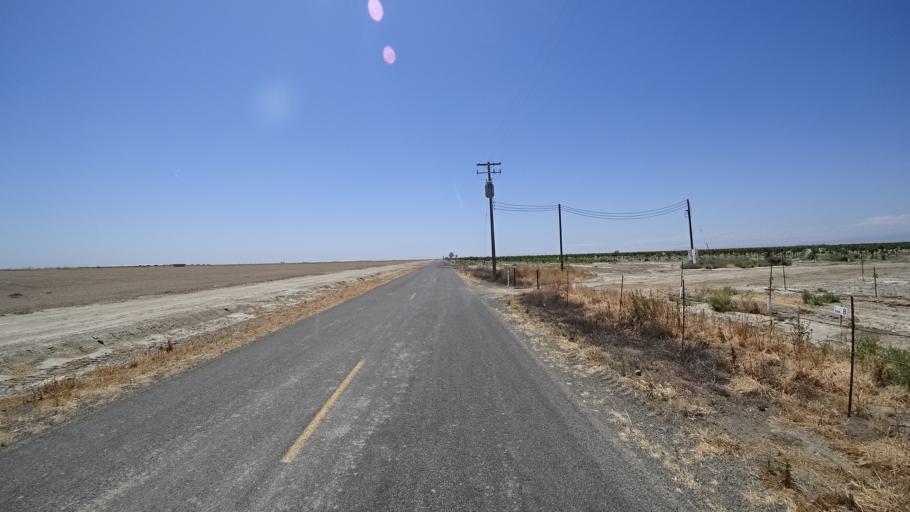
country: US
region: California
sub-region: Kings County
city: Armona
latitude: 36.2041
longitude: -119.7086
